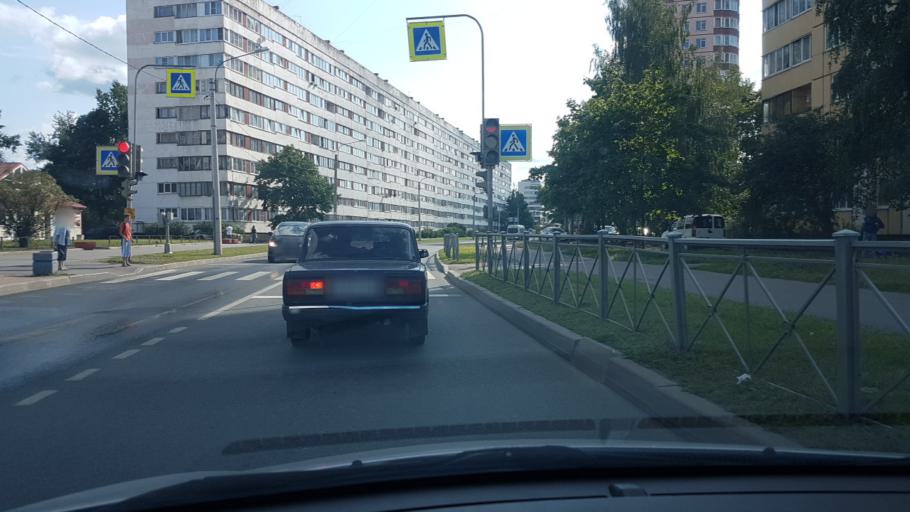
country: RU
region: St.-Petersburg
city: Sosnovaya Polyana
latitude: 59.8418
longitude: 30.1305
